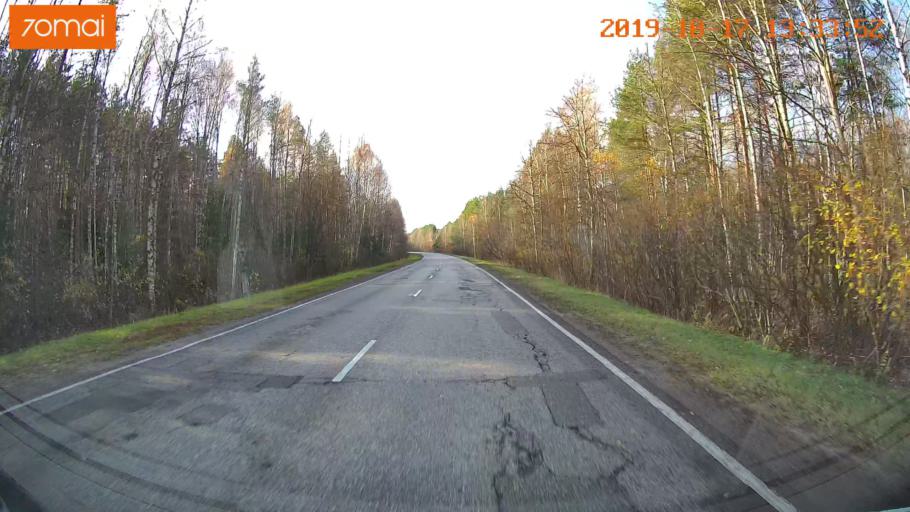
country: RU
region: Vladimir
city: Velikodvorskiy
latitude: 55.1444
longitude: 40.7309
